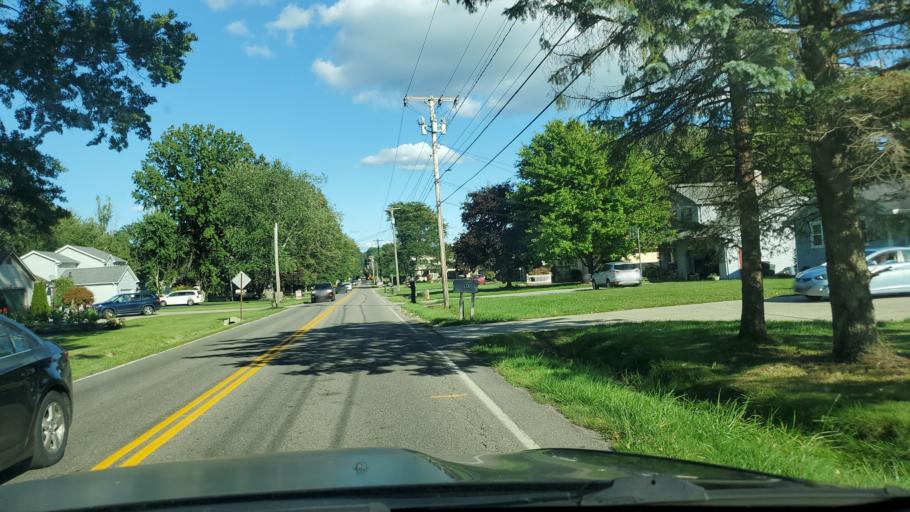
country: US
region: Ohio
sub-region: Mahoning County
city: Boardman
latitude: 41.0468
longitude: -80.7032
